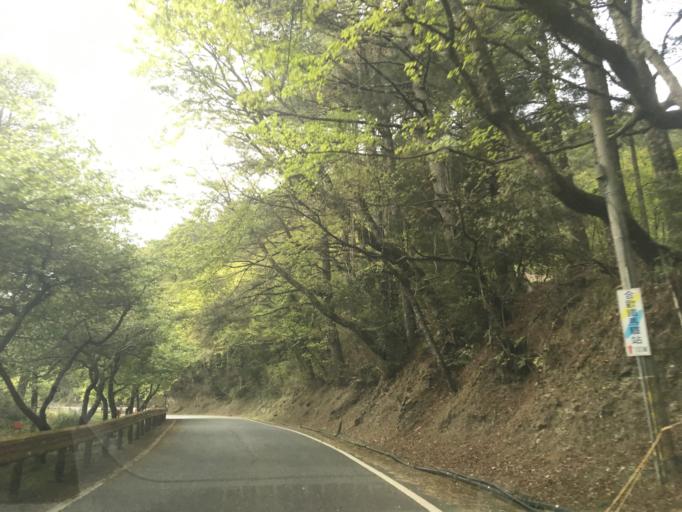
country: TW
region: Taiwan
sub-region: Hualien
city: Hualian
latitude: 24.1860
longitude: 121.3409
